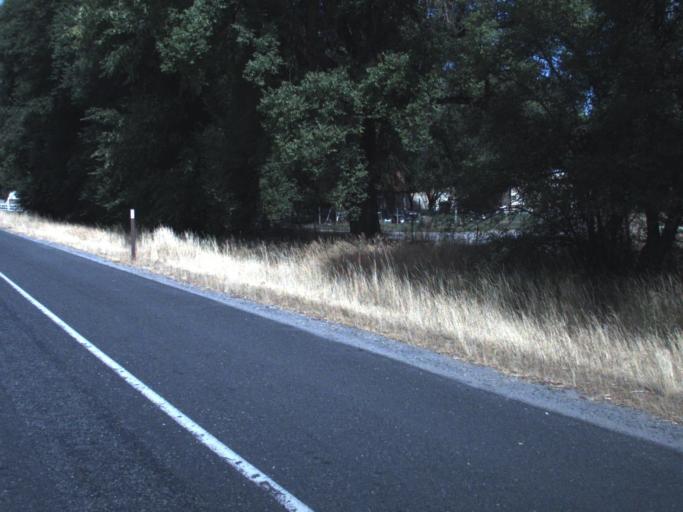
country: US
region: Washington
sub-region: Stevens County
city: Colville
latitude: 48.4527
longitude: -117.8761
